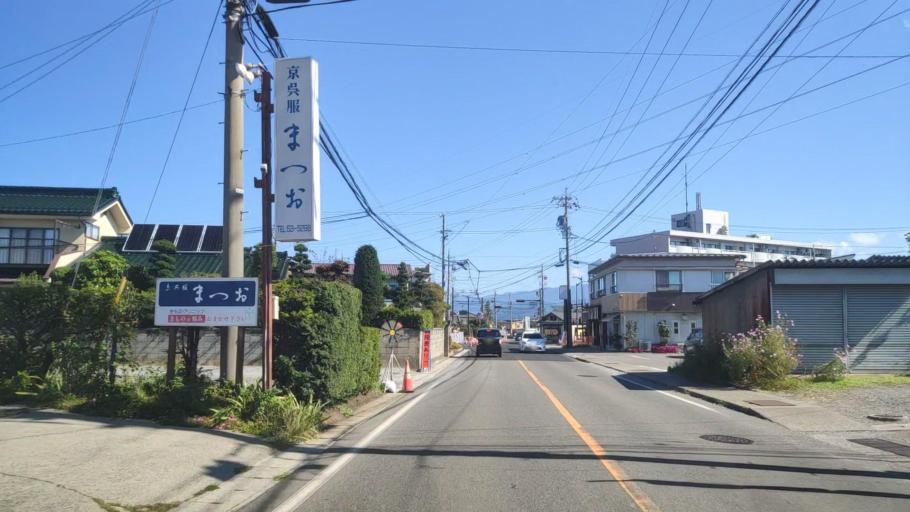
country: JP
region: Nagano
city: Shiojiri
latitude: 36.1476
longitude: 137.9452
